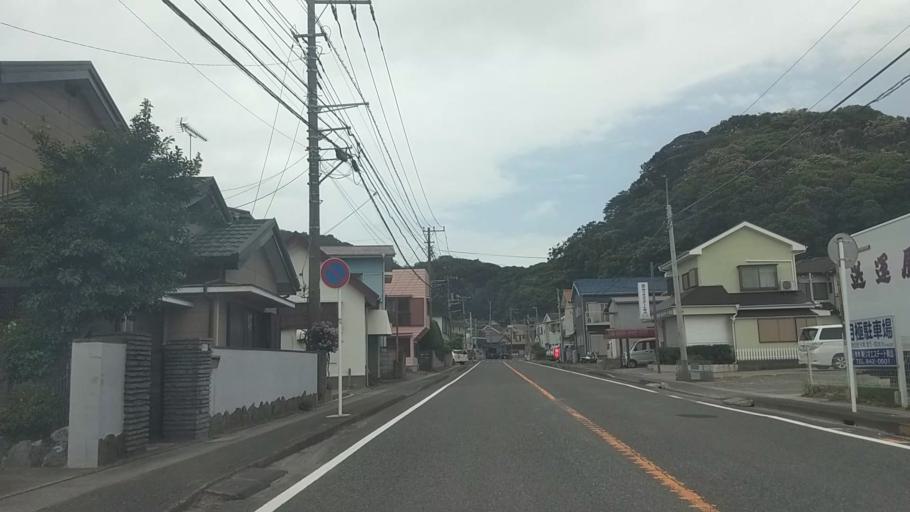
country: JP
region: Kanagawa
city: Yokosuka
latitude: 35.2519
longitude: 139.7369
